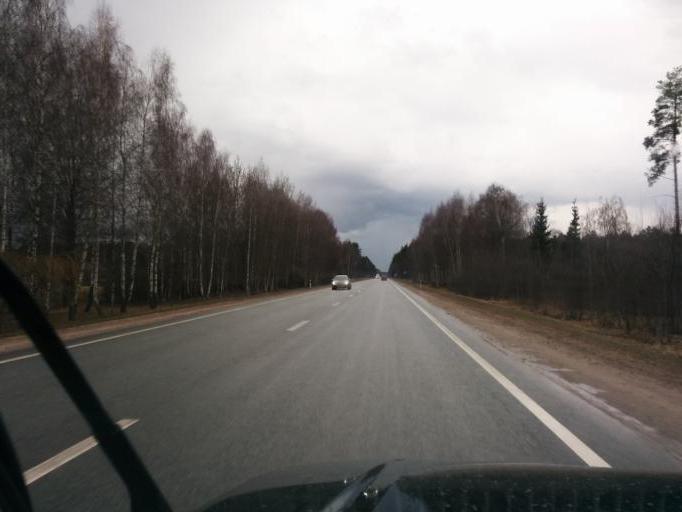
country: LV
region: Babite
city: Pinki
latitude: 56.8824
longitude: 23.9477
